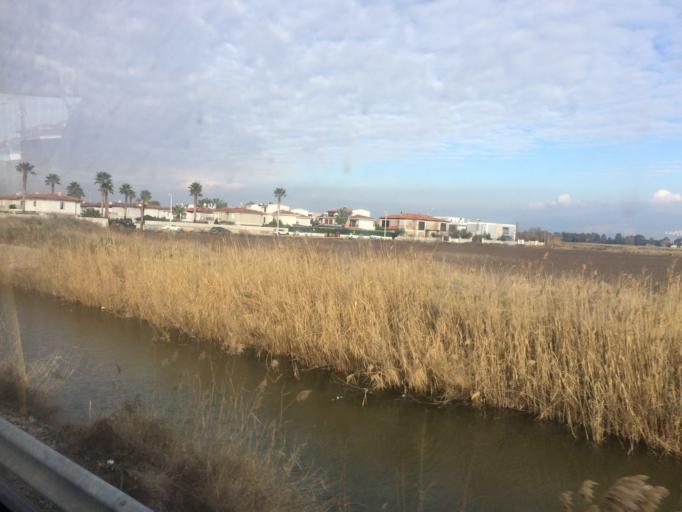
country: TR
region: Izmir
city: Menemen
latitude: 38.5005
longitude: 26.9600
